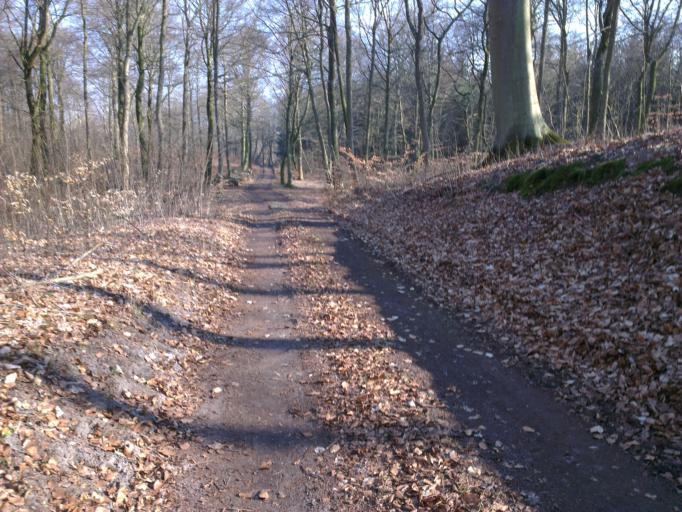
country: DK
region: Capital Region
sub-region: Frederikssund Kommune
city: Jaegerspris
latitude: 55.8932
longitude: 12.0032
